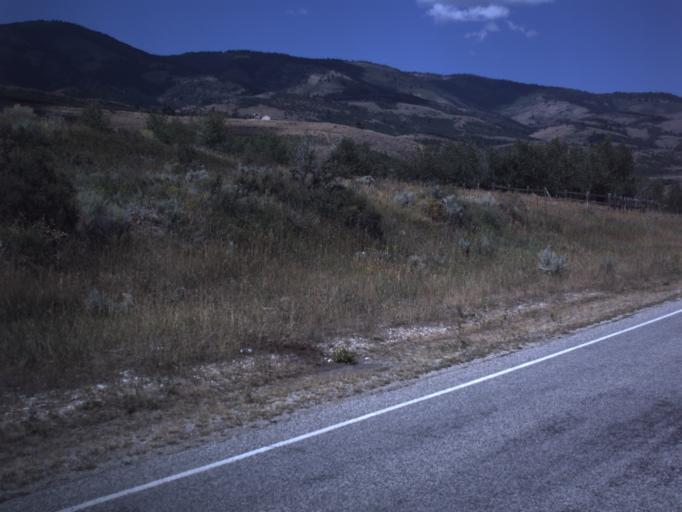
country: US
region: Idaho
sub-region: Bear Lake County
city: Paris
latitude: 41.9790
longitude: -111.4036
